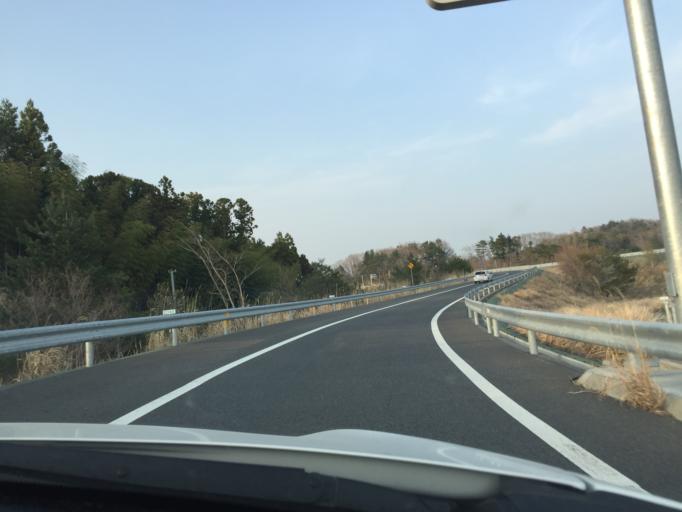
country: JP
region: Fukushima
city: Namie
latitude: 37.3751
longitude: 140.9649
